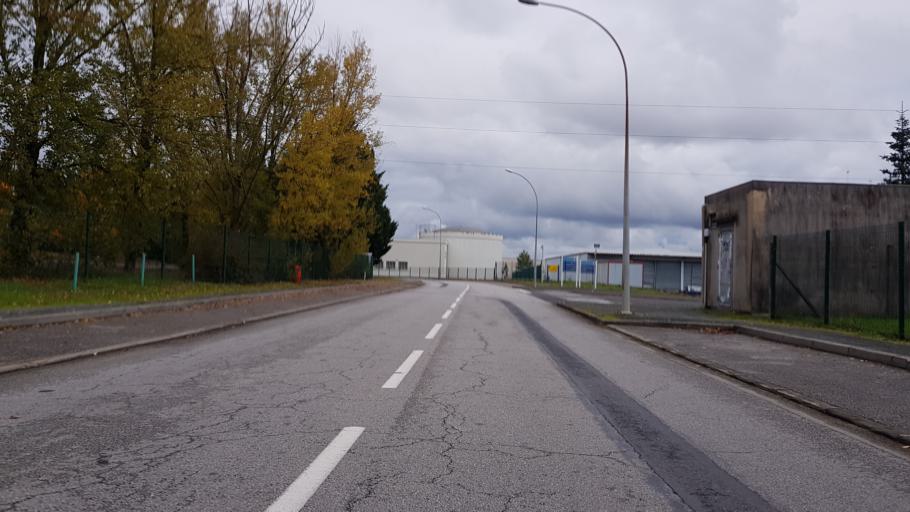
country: FR
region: Poitou-Charentes
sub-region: Departement de la Vienne
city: Chasseneuil-du-Poitou
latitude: 46.6614
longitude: 0.3730
